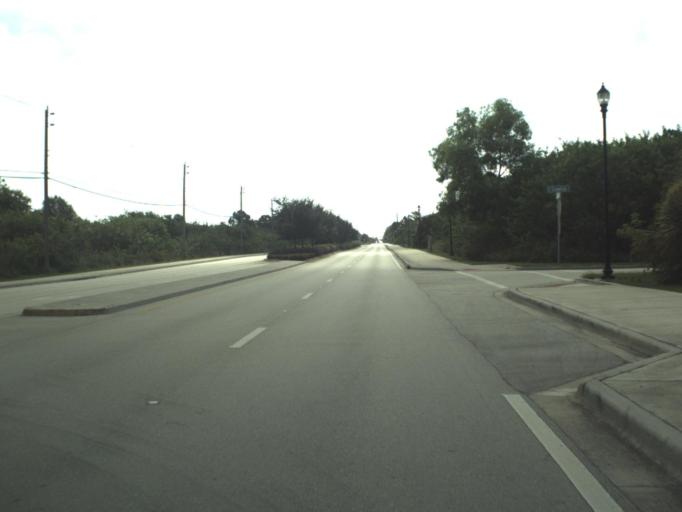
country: US
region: Florida
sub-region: Saint Lucie County
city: Port Saint Lucie
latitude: 27.2095
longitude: -80.3661
